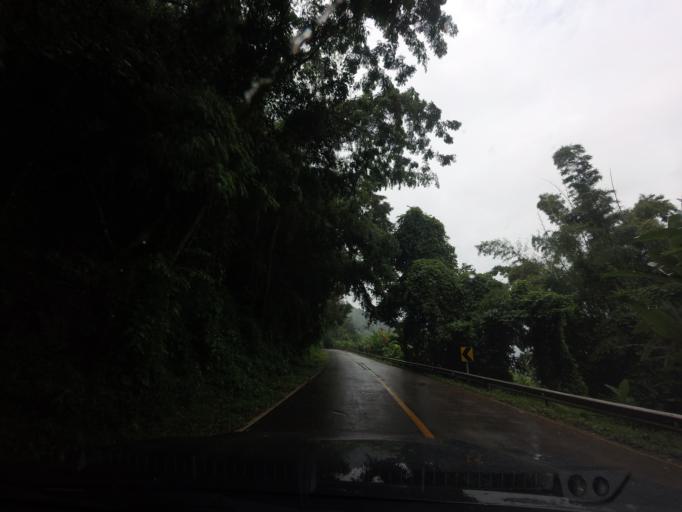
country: TH
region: Nong Khai
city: Sangkhom
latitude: 18.2077
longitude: 102.1055
